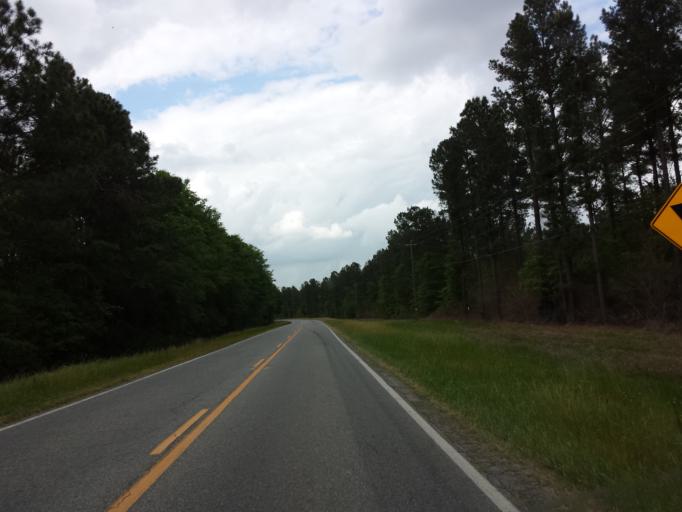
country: US
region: Georgia
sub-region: Cook County
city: Sparks
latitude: 31.2056
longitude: -83.4503
